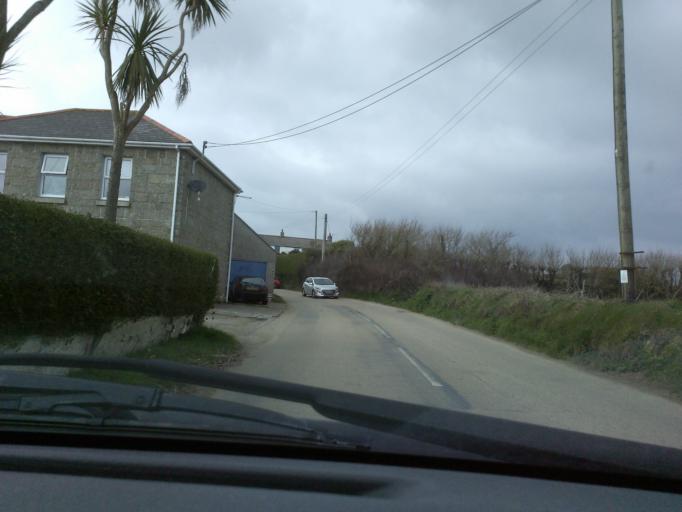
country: GB
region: England
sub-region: Cornwall
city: Sennen
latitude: 50.0571
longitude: -5.6666
